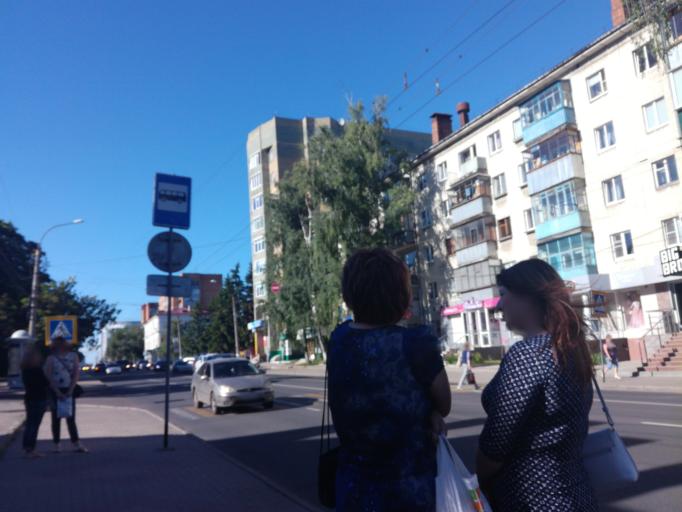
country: RU
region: Kursk
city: Kursk
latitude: 51.7439
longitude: 36.1901
